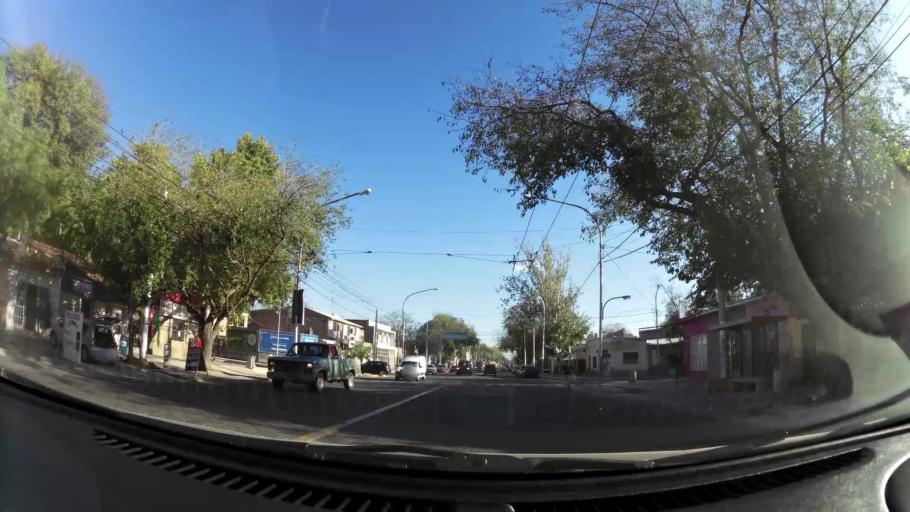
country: AR
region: Mendoza
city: Las Heras
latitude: -32.8617
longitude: -68.8328
